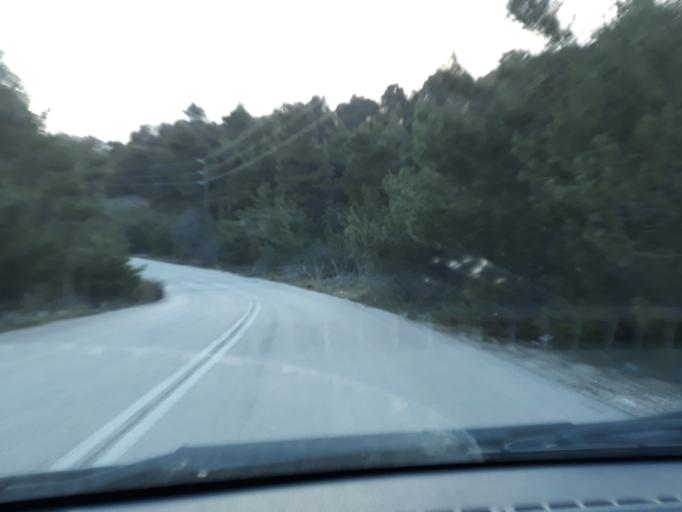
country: GR
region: Attica
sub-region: Nomarchia Anatolikis Attikis
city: Afidnes
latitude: 38.2117
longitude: 23.8019
